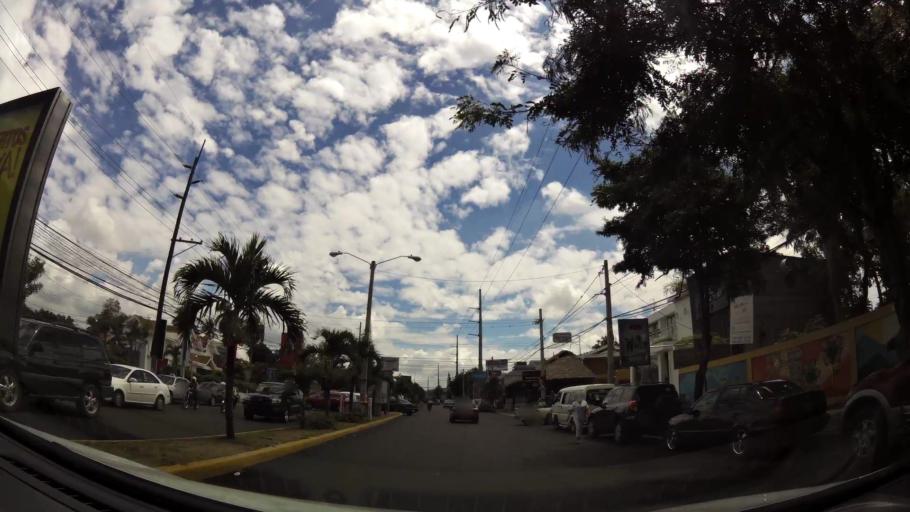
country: DO
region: Santiago
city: Santiago de los Caballeros
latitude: 19.4588
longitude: -70.6792
